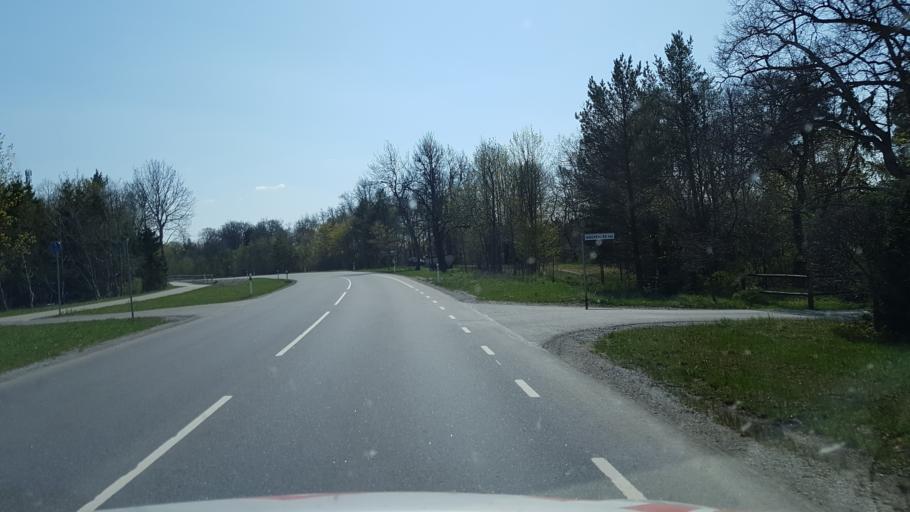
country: EE
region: Harju
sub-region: Paldiski linn
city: Paldiski
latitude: 59.3847
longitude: 24.2359
